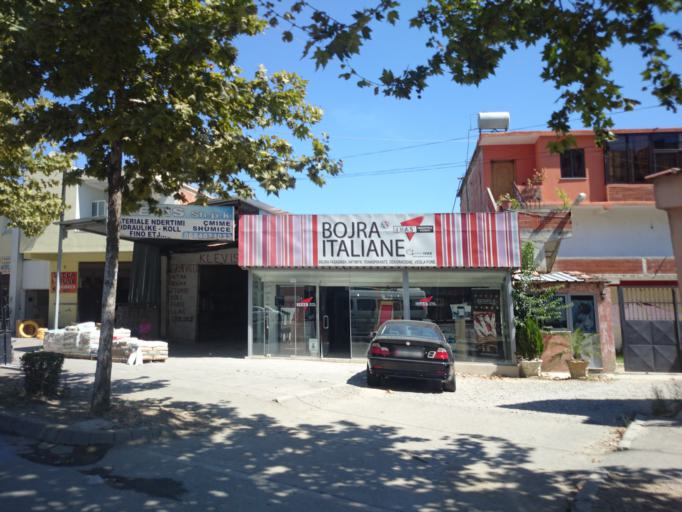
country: AL
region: Tirane
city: Tirana
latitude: 41.3271
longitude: 19.7867
